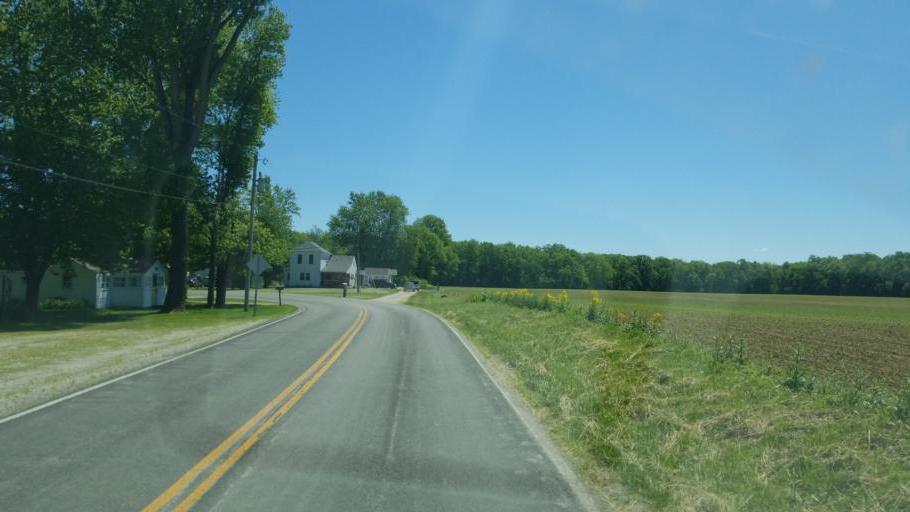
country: US
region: Ohio
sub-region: Shelby County
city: Fort Loramie
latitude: 40.3667
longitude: -84.3377
